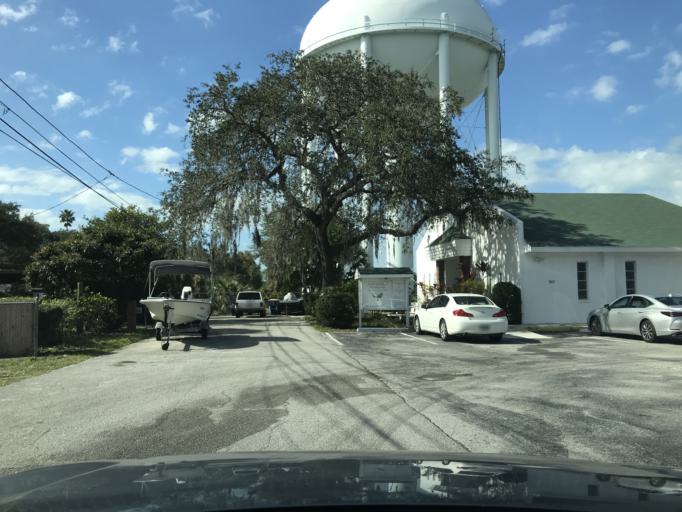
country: US
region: Florida
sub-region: Pinellas County
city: Belleair
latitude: 27.9448
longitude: -82.7902
